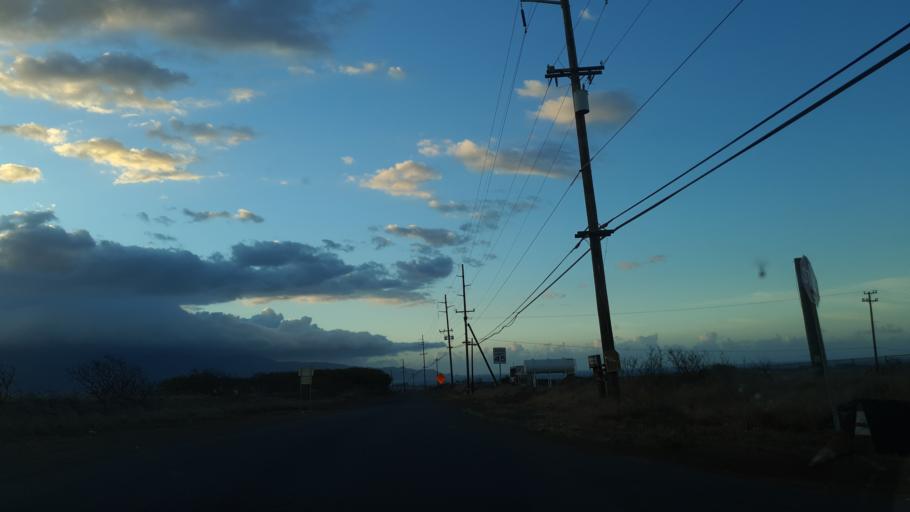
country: US
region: Hawaii
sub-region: Maui County
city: Kahului
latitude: 20.8582
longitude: -156.4244
